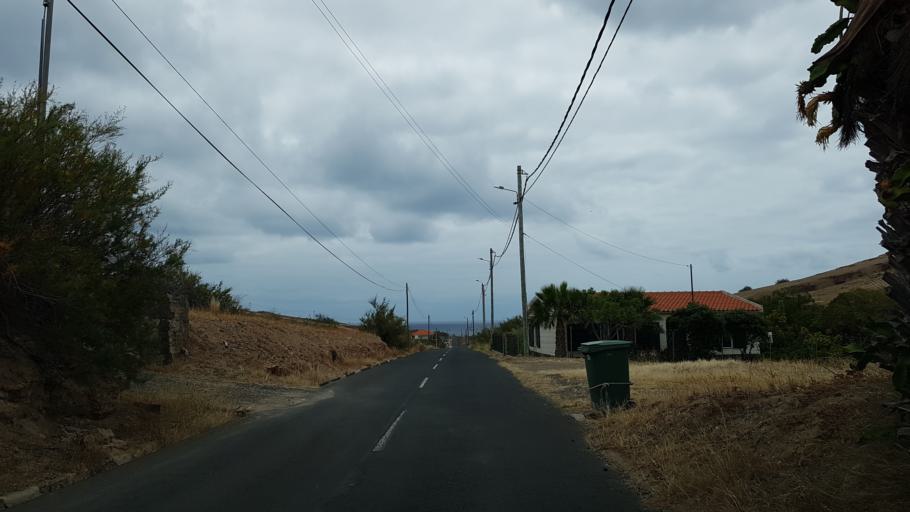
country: PT
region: Madeira
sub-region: Porto Santo
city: Vila de Porto Santo
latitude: 33.0716
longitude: -16.3033
